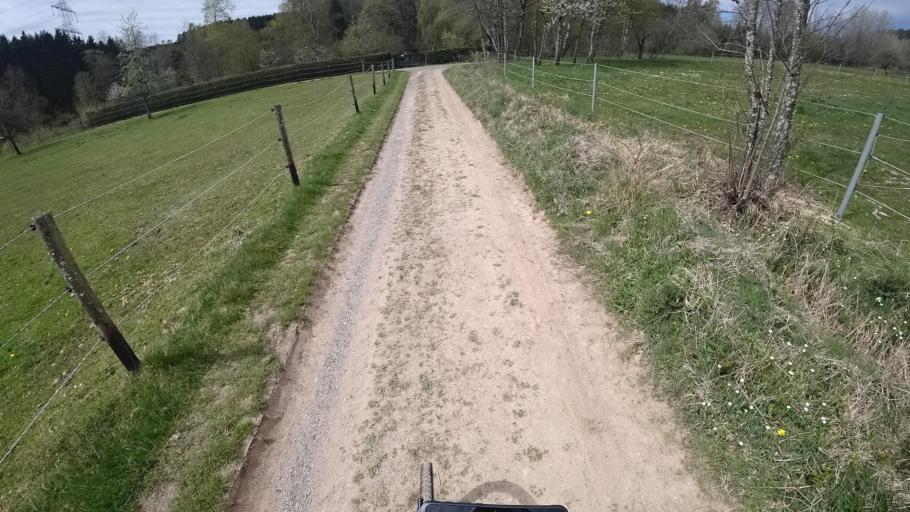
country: DE
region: Rheinland-Pfalz
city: Gusenburg
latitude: 49.6346
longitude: 6.8945
